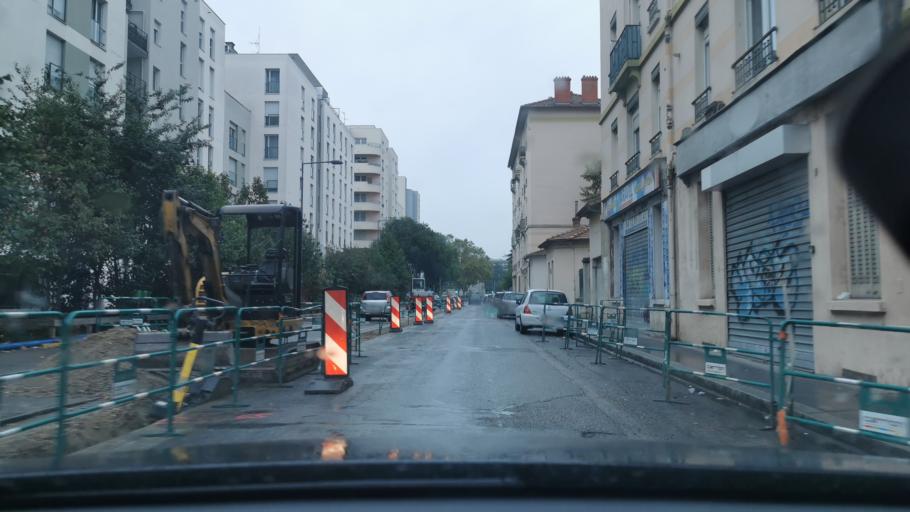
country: FR
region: Rhone-Alpes
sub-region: Departement du Rhone
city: Villeurbanne
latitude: 45.7747
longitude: 4.8741
